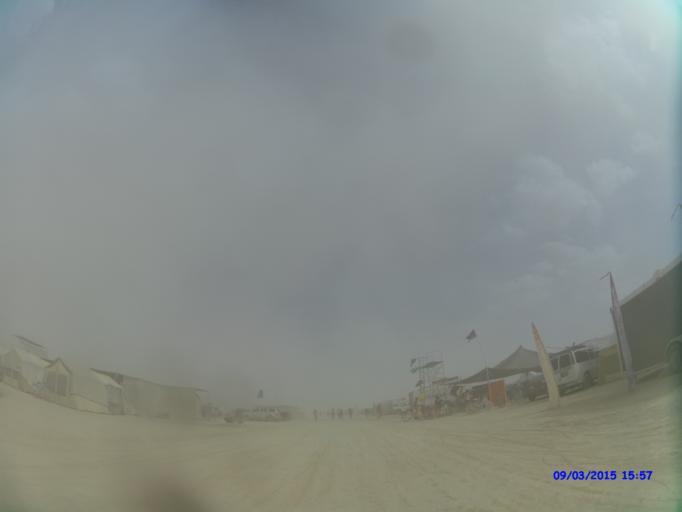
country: US
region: Nevada
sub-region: Pershing County
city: Lovelock
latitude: 40.7781
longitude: -119.2123
